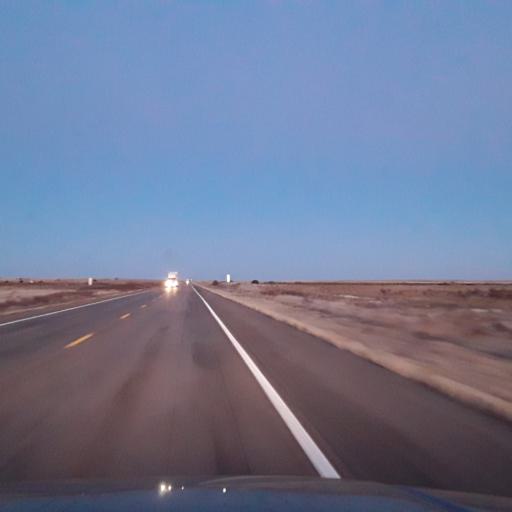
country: US
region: New Mexico
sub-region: Guadalupe County
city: Santa Rosa
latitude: 34.7581
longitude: -104.9948
